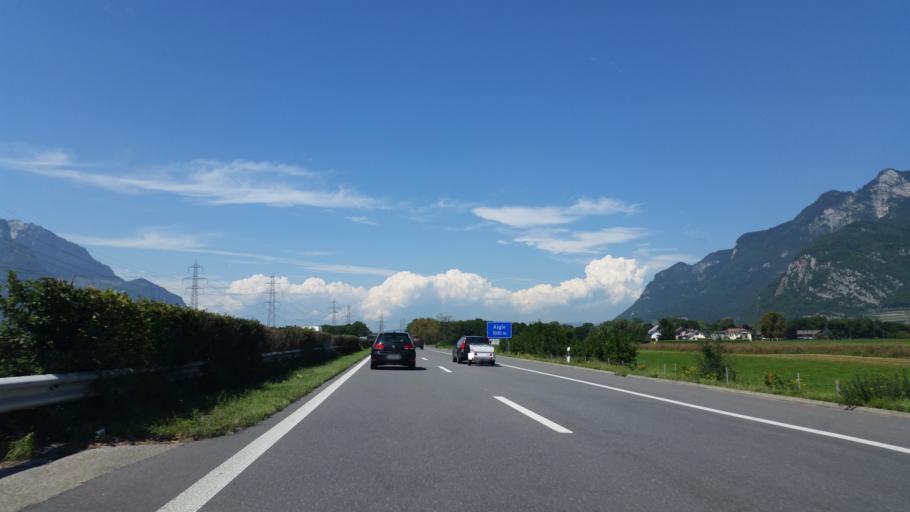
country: CH
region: Vaud
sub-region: Aigle District
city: Aigle
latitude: 46.3090
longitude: 6.9496
